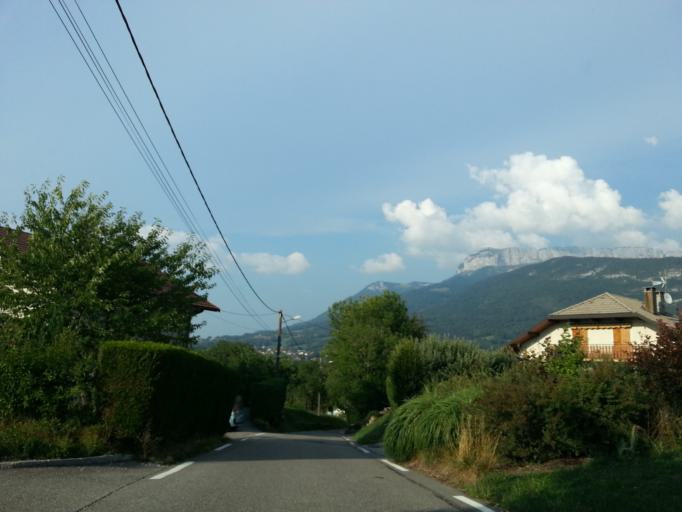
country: FR
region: Rhone-Alpes
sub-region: Departement de la Haute-Savoie
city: Annecy-le-Vieux
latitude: 45.9193
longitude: 6.1723
